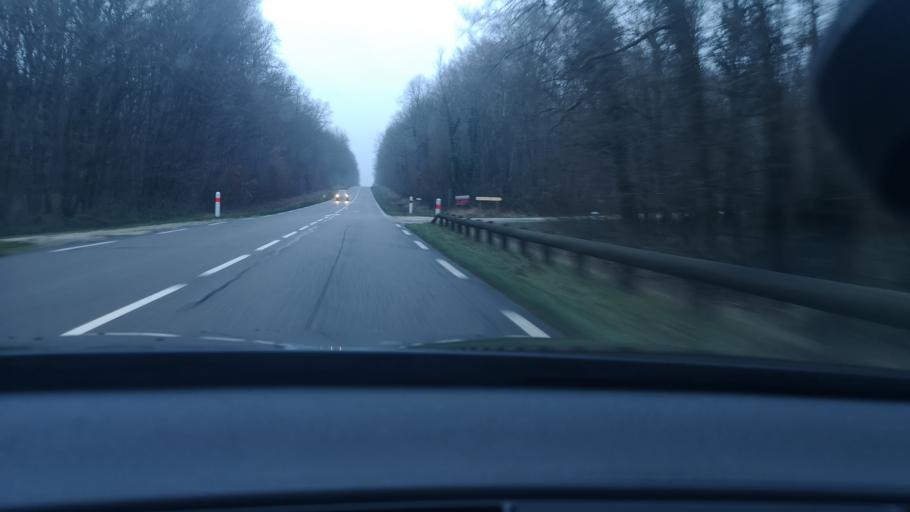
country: FR
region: Bourgogne
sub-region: Departement de la Cote-d'Or
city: Aiserey
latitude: 47.1099
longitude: 5.1015
